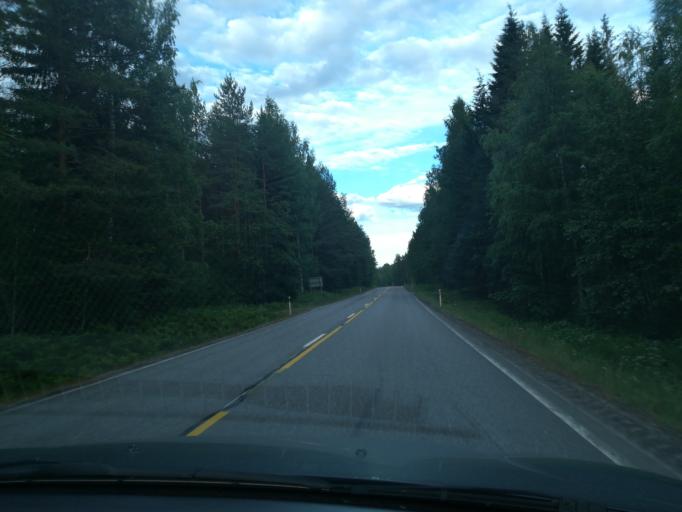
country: FI
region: Southern Savonia
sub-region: Mikkeli
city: Puumala
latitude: 61.5658
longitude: 28.0870
